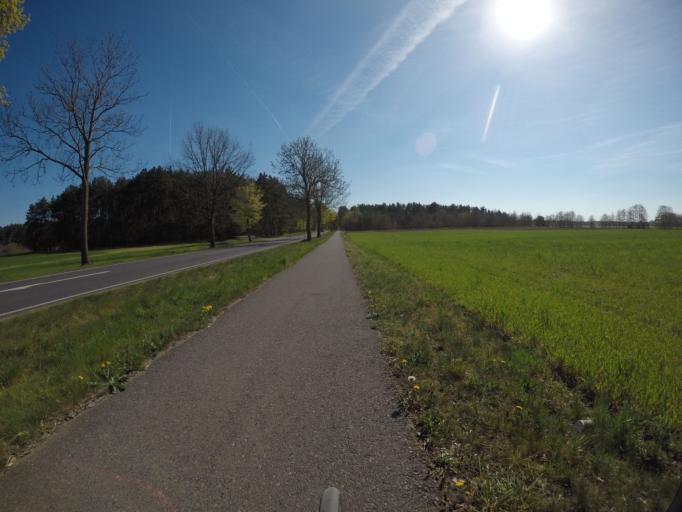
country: DE
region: Brandenburg
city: Rehfelde
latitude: 52.4898
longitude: 13.9161
